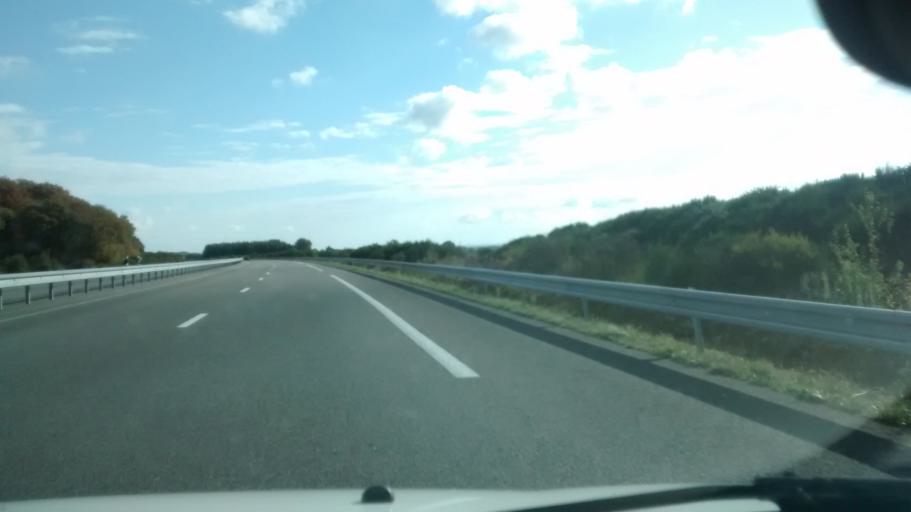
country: FR
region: Pays de la Loire
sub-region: Departement de Maine-et-Loire
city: Combree
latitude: 47.7245
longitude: -1.0534
